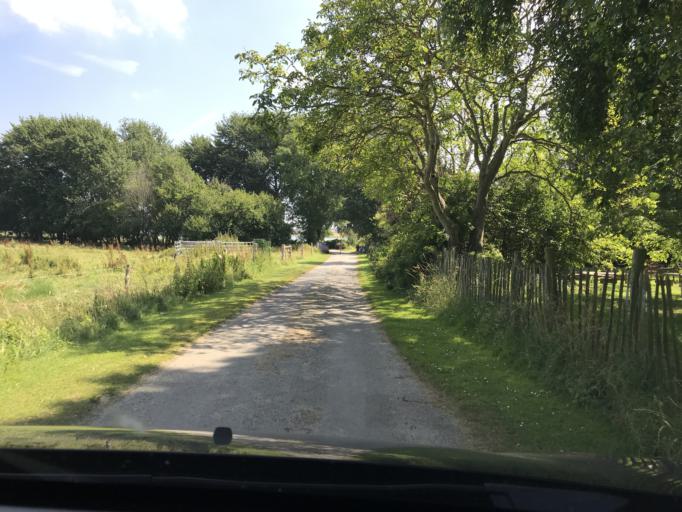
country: DK
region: South Denmark
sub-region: AEro Kommune
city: AEroskobing
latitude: 54.8851
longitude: 10.3679
